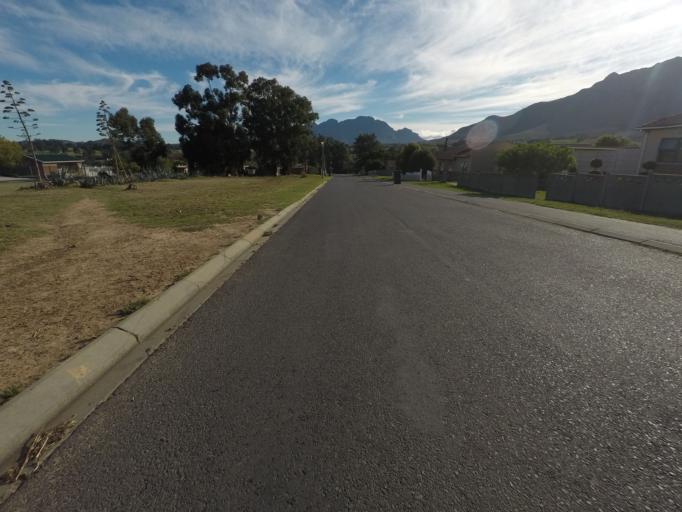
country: ZA
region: Western Cape
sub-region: Cape Winelands District Municipality
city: Stellenbosch
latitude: -33.9775
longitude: 18.8438
